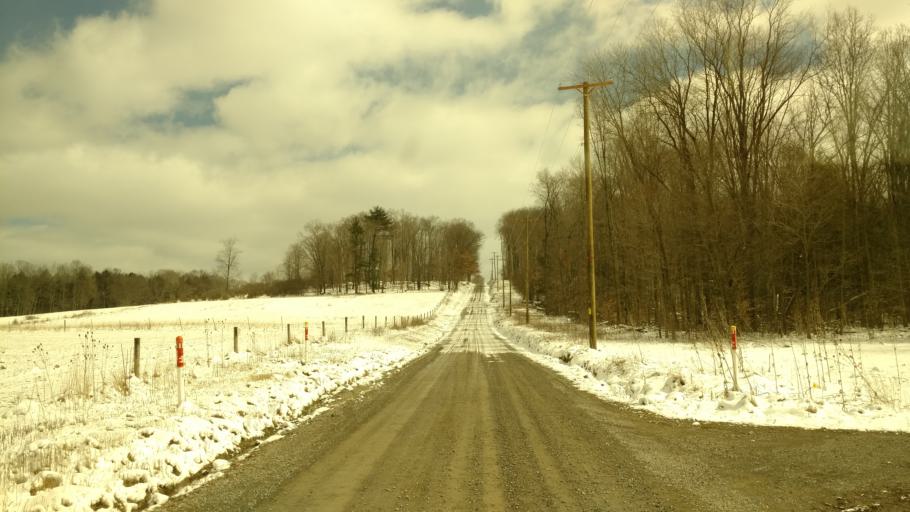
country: US
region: Pennsylvania
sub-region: Mercer County
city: Mercer
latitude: 41.3298
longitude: -80.2419
